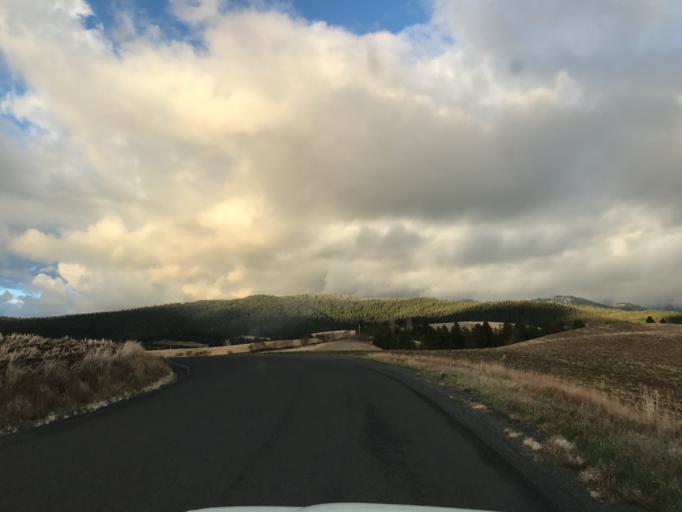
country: US
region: Idaho
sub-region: Latah County
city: Moscow
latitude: 46.7843
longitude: -116.9624
